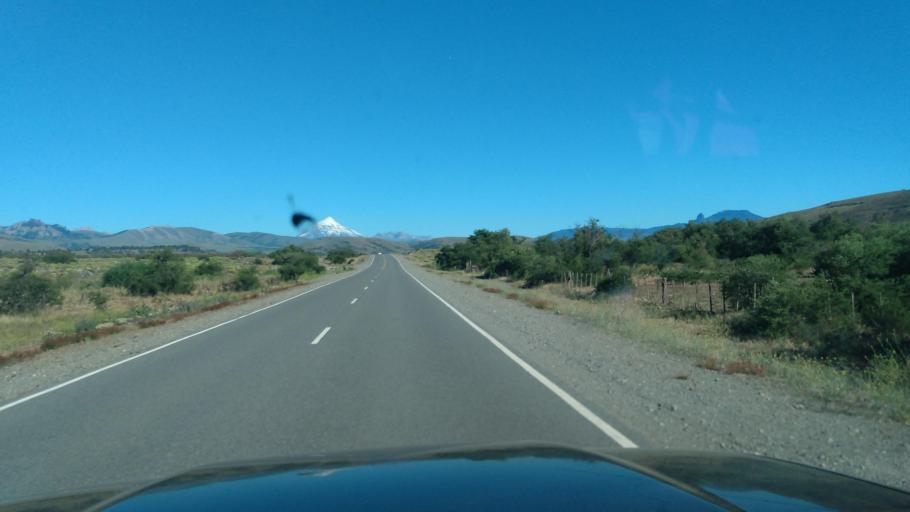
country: AR
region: Neuquen
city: Junin de los Andes
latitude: -39.8857
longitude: -71.1577
